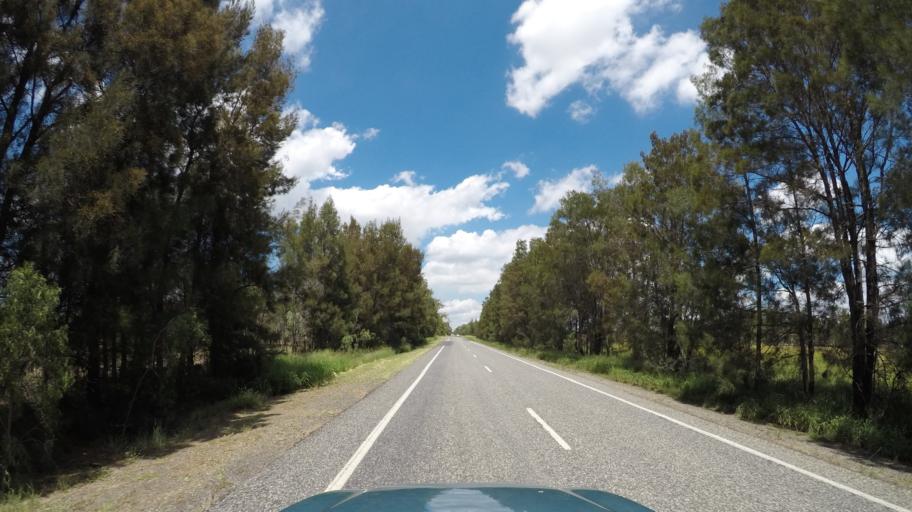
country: AU
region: Queensland
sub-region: Toowoomba
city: Oakey
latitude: -27.8926
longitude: 151.2113
